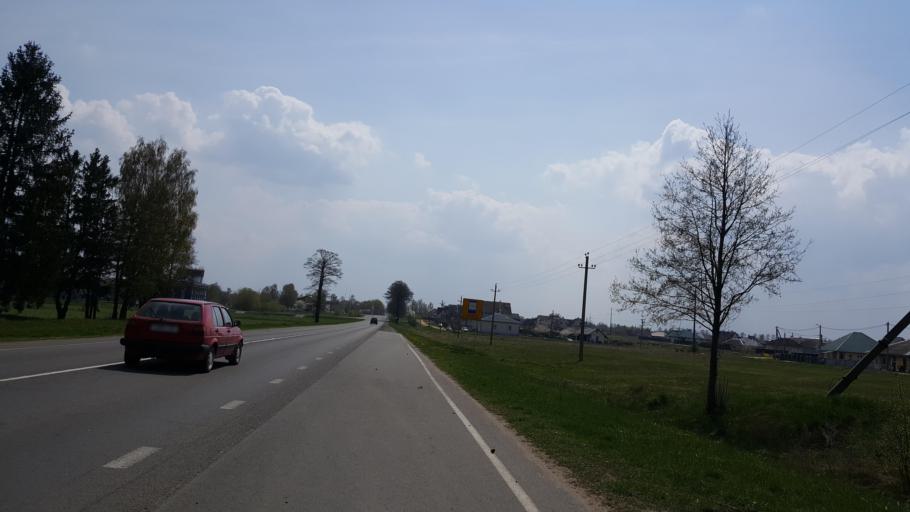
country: BY
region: Brest
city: Zhabinka
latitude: 52.2100
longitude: 24.0010
